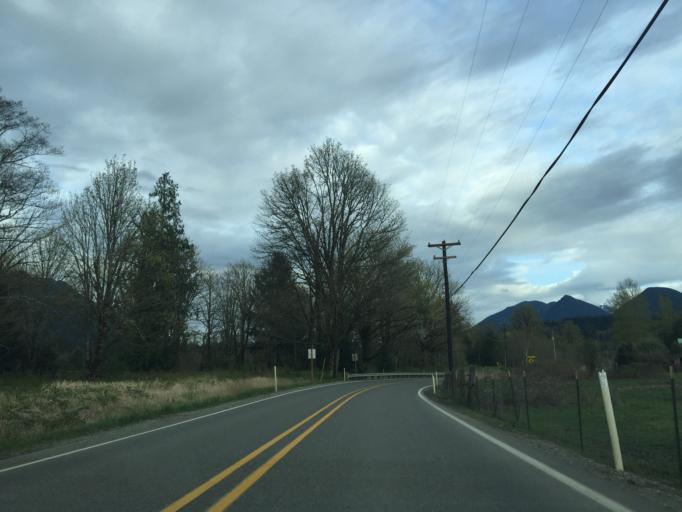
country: US
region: Washington
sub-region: Snohomish County
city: Arlington Heights
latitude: 48.2721
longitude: -121.8915
